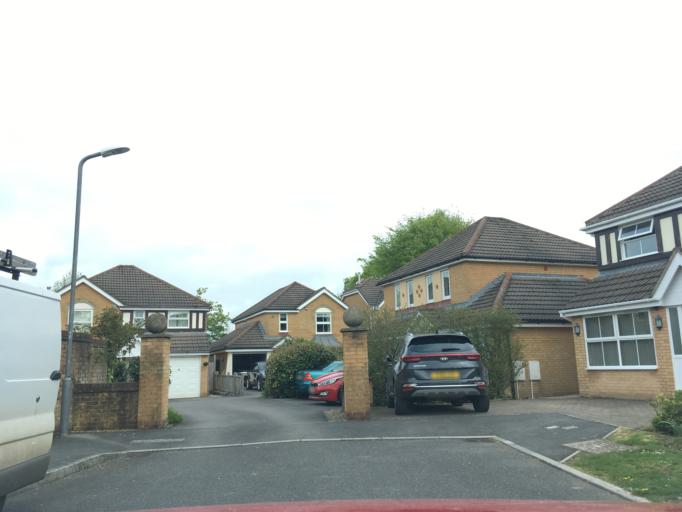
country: GB
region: England
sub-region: Bath and North East Somerset
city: Clutton
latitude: 51.3279
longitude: -2.5187
